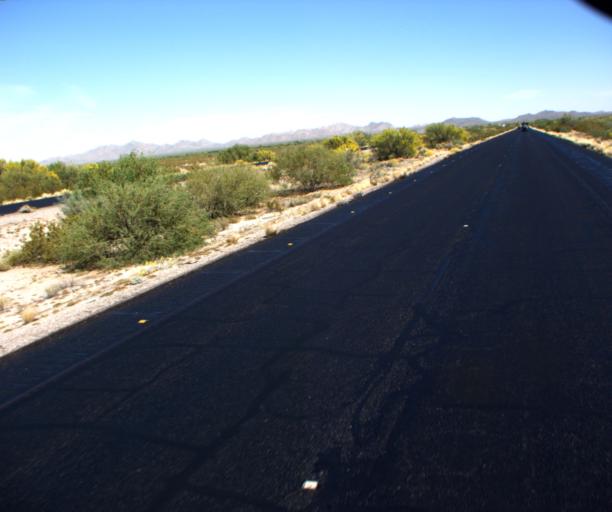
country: US
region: Arizona
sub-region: Pinal County
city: Maricopa
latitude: 32.8438
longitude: -112.2708
